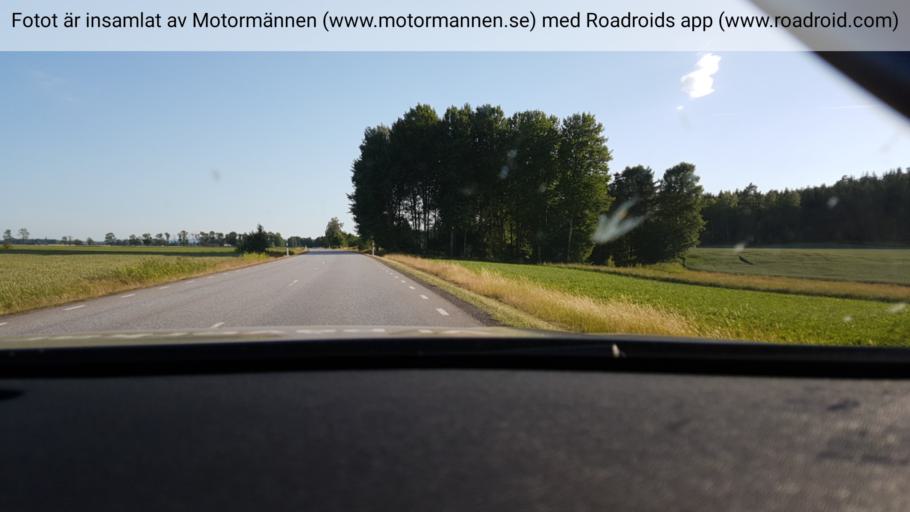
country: SE
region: Vaestra Goetaland
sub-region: Toreboda Kommun
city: Toereboda
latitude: 58.6382
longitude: 14.0284
